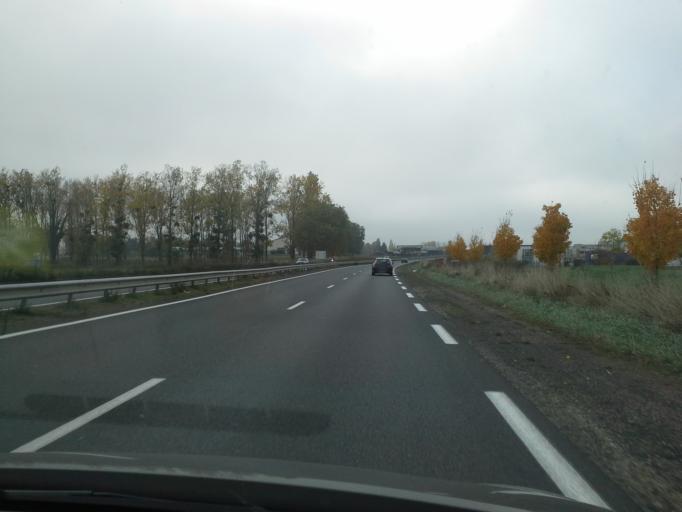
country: FR
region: Centre
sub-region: Departement d'Indre-et-Loire
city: Parcay-Meslay
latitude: 47.4425
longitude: 0.7197
